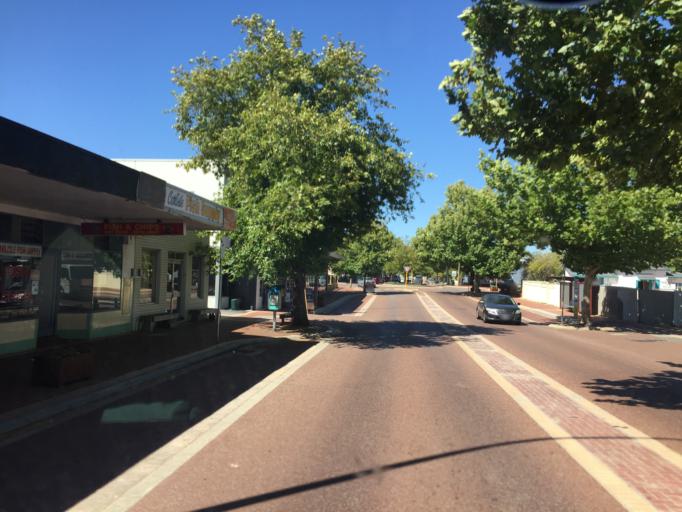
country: AU
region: Western Australia
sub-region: Victoria Park
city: Victoria Park
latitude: -31.9781
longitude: 115.9114
